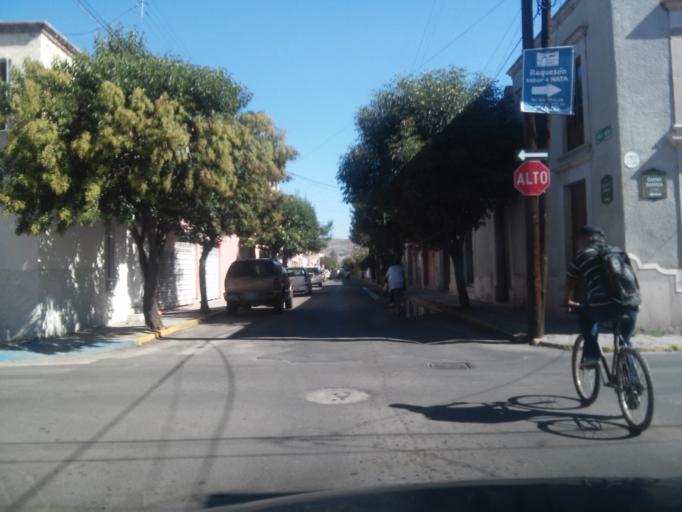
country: MX
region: Durango
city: Victoria de Durango
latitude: 24.0298
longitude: -104.6692
